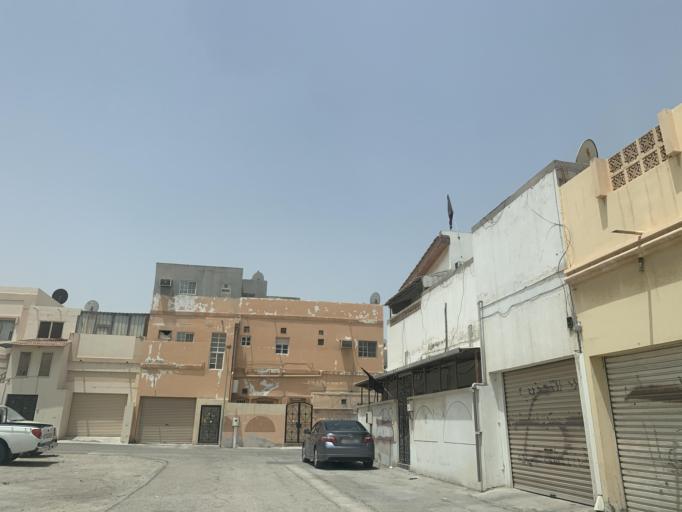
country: BH
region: Northern
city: Madinat `Isa
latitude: 26.1527
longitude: 50.5207
